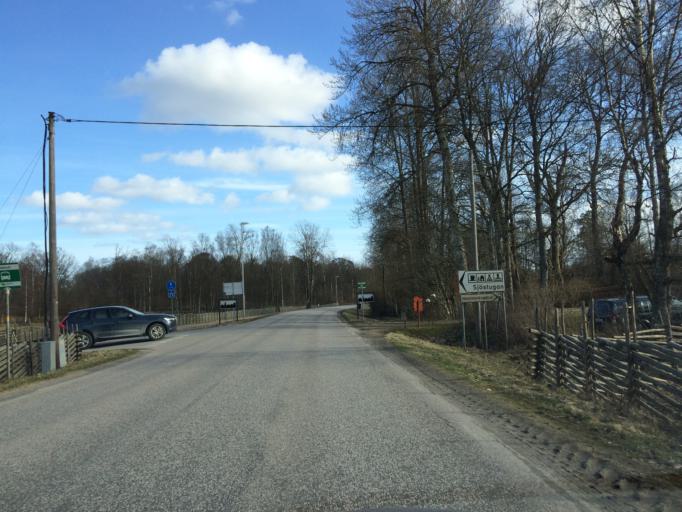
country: SE
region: Kronoberg
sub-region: Almhults Kommun
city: AElmhult
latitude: 56.5665
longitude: 14.1257
